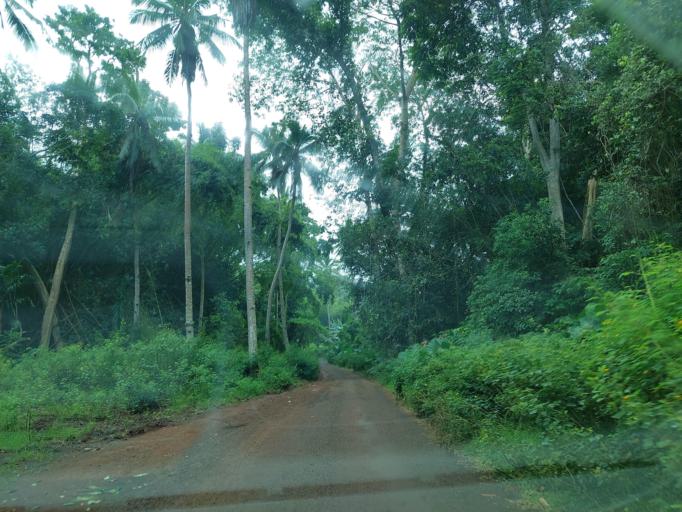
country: YT
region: Tsingoni
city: Tsingoni
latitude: -12.7592
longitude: 45.1247
